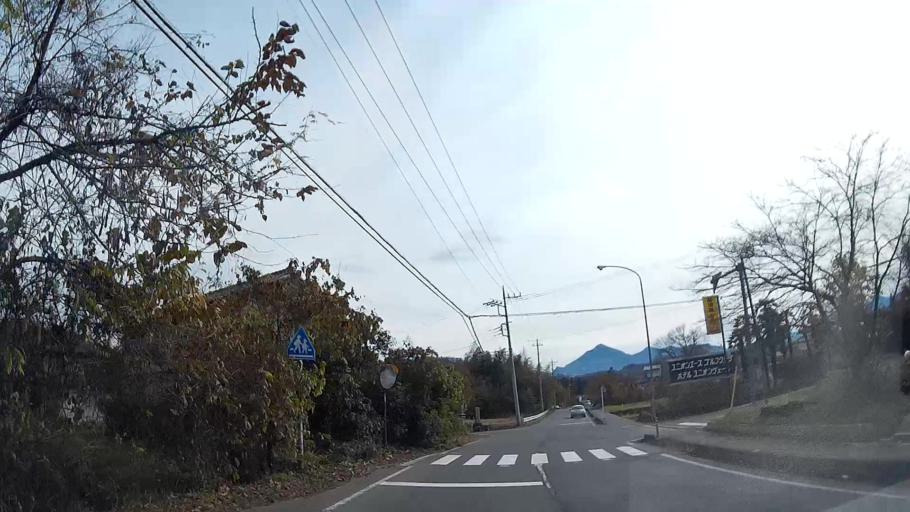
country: JP
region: Saitama
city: Chichibu
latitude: 36.0295
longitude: 139.0365
